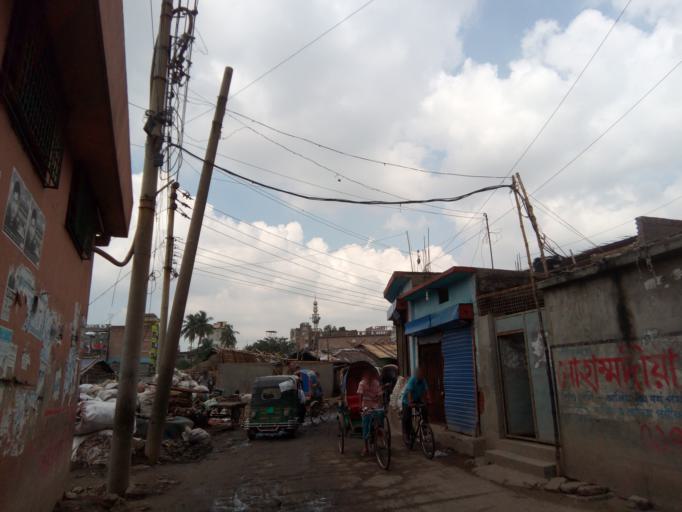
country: BD
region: Dhaka
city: Azimpur
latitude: 23.7332
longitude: 90.3637
